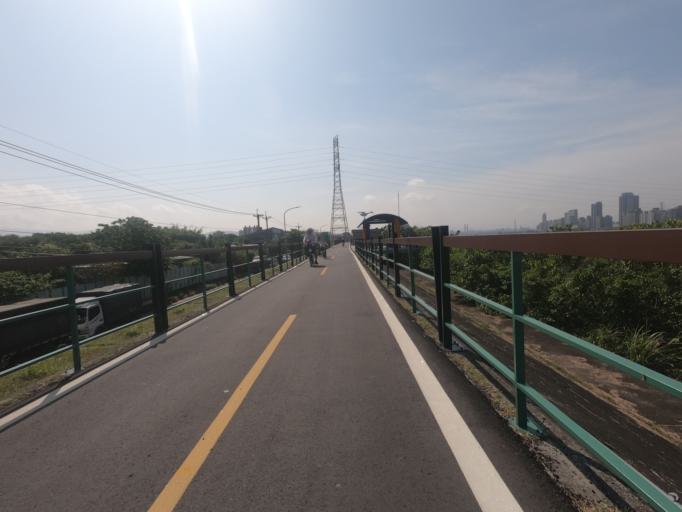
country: TW
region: Taipei
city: Taipei
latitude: 25.1008
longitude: 121.4875
